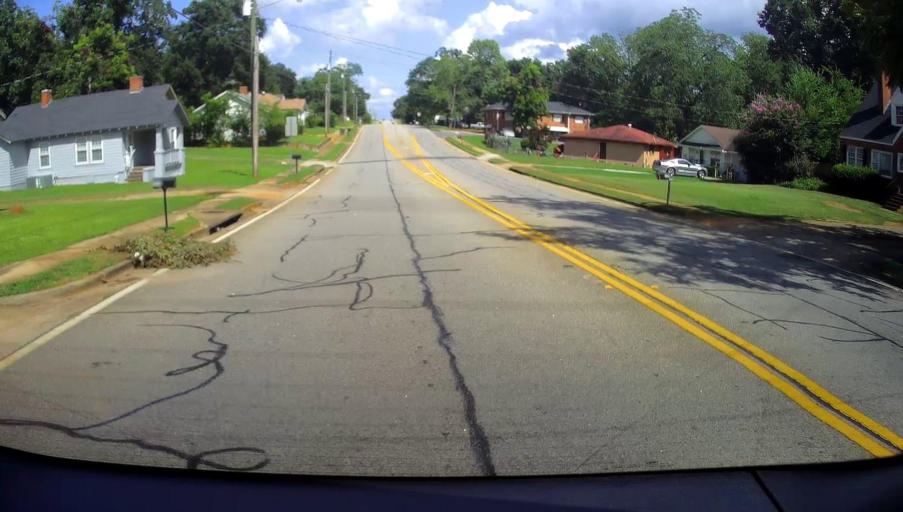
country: US
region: Georgia
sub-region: Upson County
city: Thomaston
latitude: 32.8880
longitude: -84.3217
